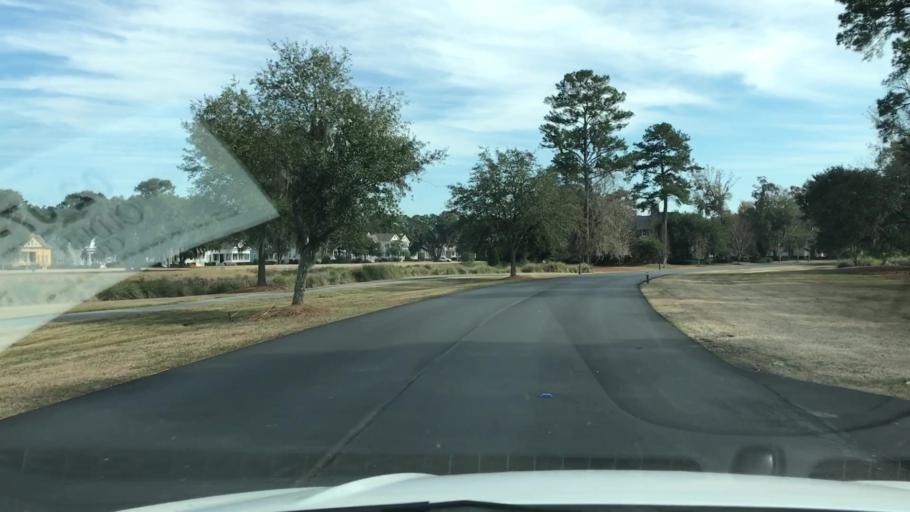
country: US
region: South Carolina
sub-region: Beaufort County
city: Bluffton
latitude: 32.3413
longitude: -80.9131
